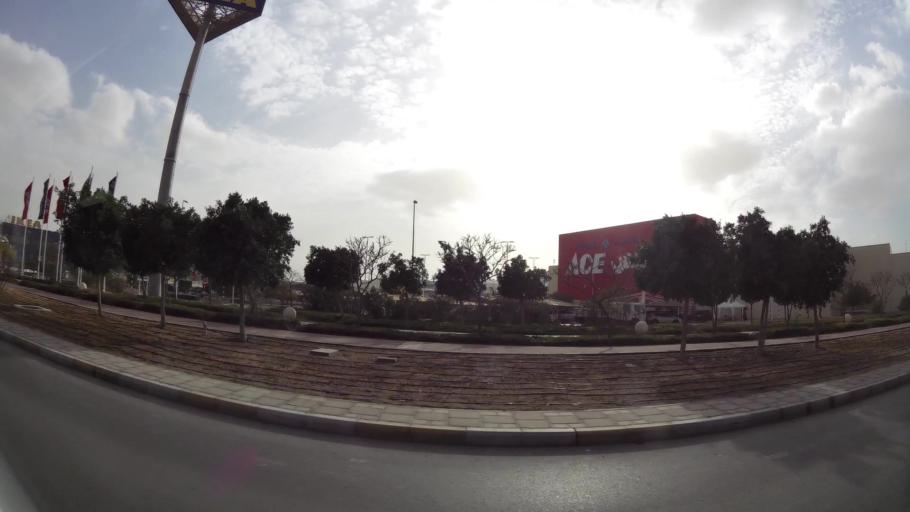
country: AE
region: Abu Dhabi
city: Abu Dhabi
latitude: 24.4920
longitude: 54.6137
